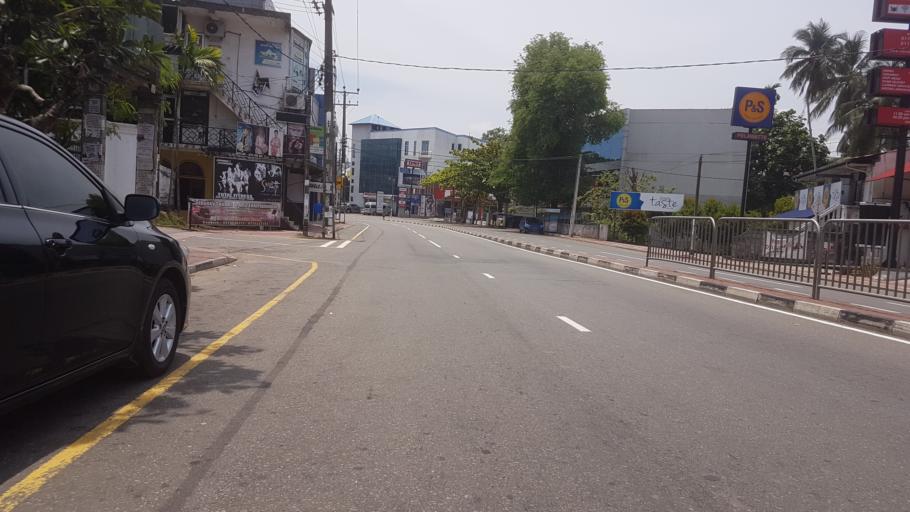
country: LK
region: Western
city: Battaramulla South
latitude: 6.8895
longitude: 79.9296
